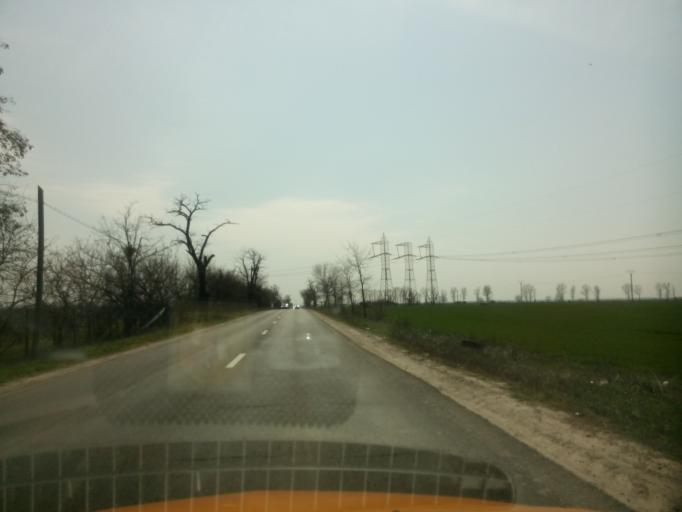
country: RO
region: Giurgiu
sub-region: Comuna Herasti
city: Herasti
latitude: 44.2540
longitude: 26.3652
